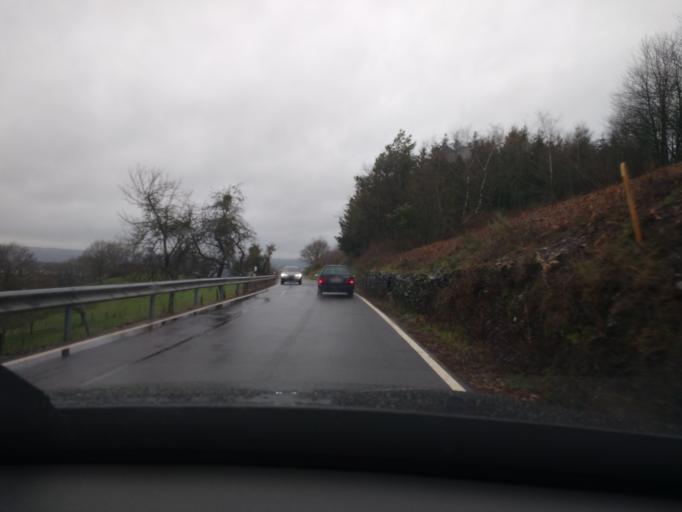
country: DE
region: Rheinland-Pfalz
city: Irsch
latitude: 49.7171
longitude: 6.6956
